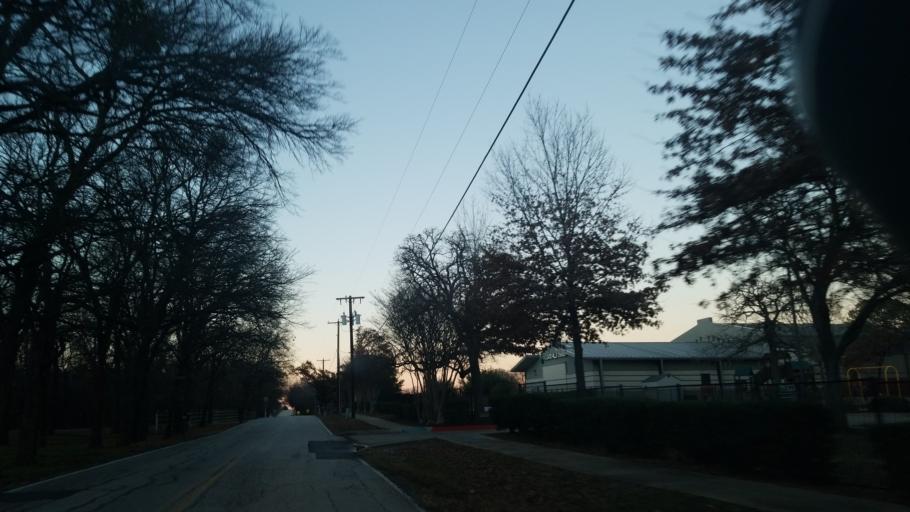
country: US
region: Texas
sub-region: Denton County
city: Hickory Creek
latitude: 33.1334
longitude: -97.0560
